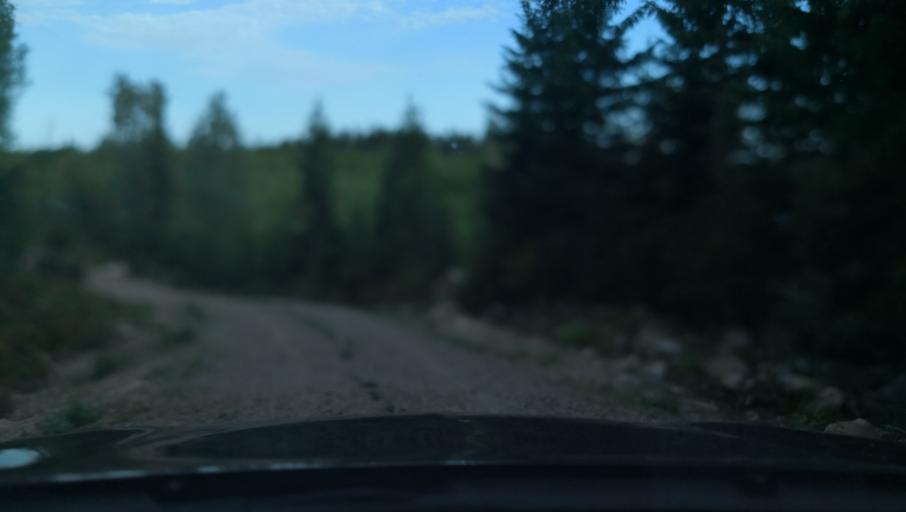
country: SE
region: Dalarna
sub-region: Smedjebackens Kommun
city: Smedjebacken
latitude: 60.0609
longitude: 15.3104
